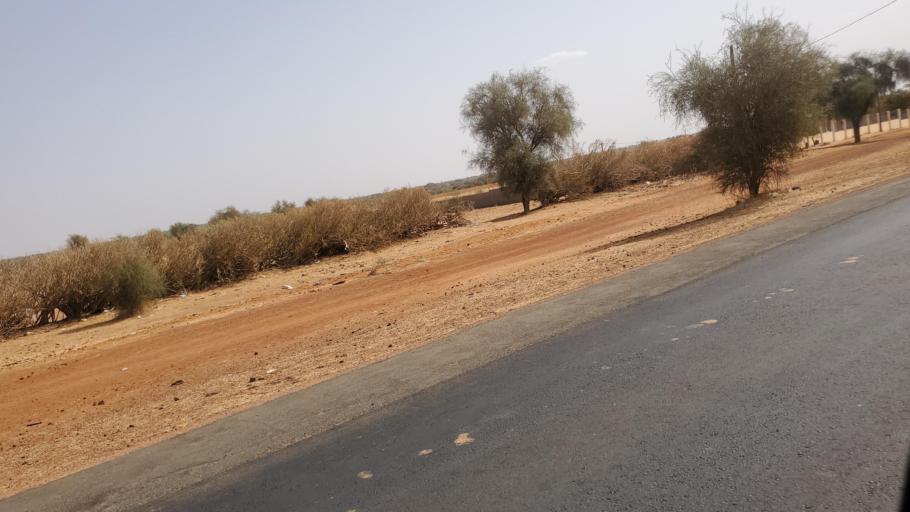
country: SN
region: Louga
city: Ndibene Dahra
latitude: 15.3986
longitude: -15.1339
